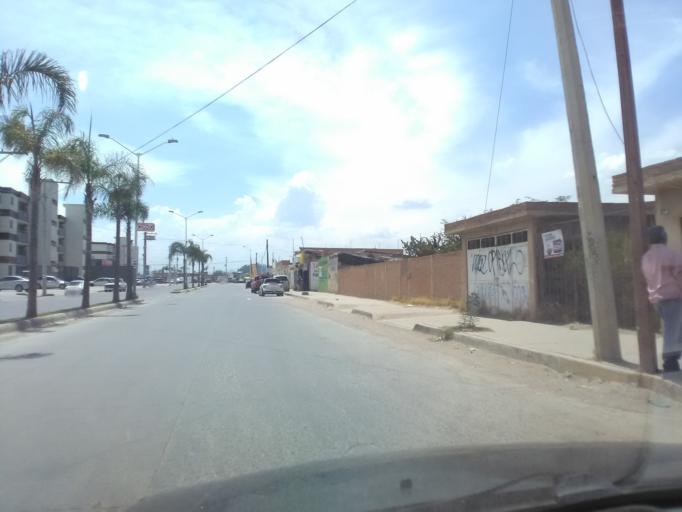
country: MX
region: Durango
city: Victoria de Durango
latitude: 24.0130
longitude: -104.6138
